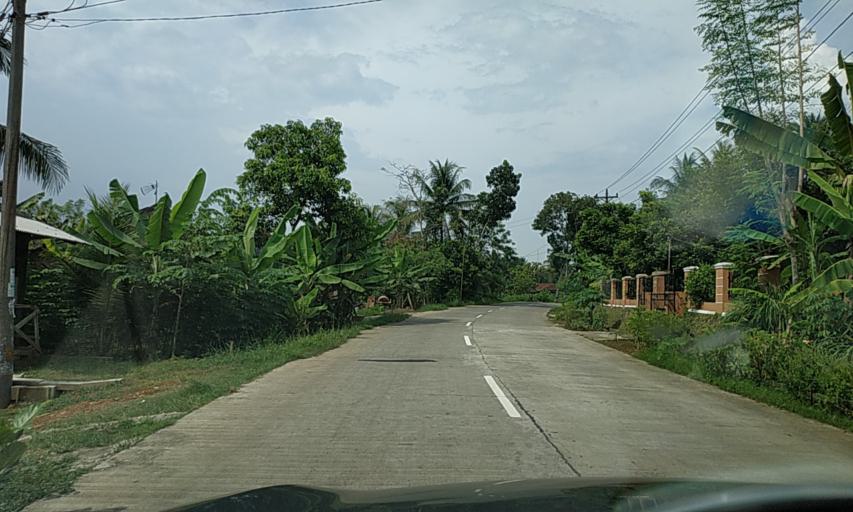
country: ID
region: Central Java
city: Winangun
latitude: -7.3569
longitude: 108.7025
